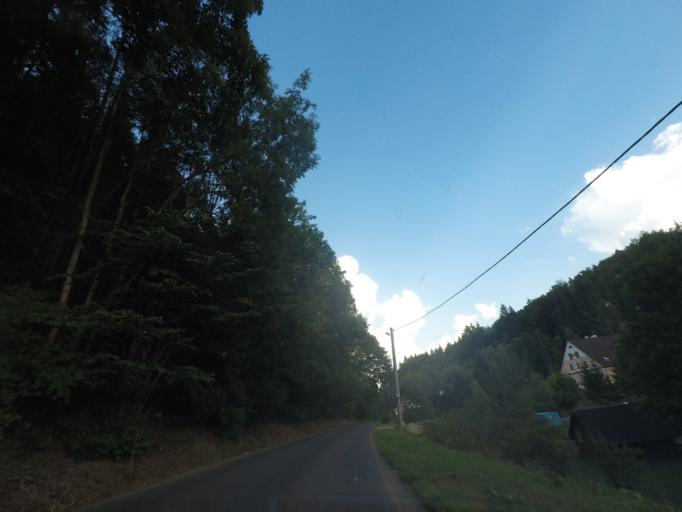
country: CZ
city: Radvanice
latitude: 50.6243
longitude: 16.0898
